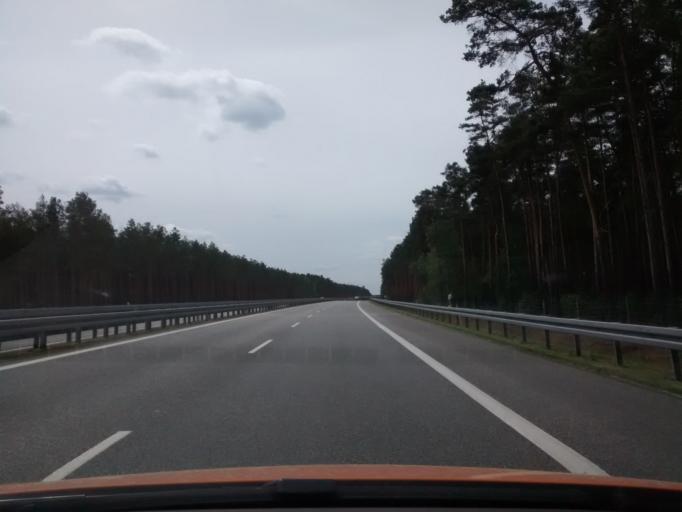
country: DE
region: Brandenburg
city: Trebbin
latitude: 52.1517
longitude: 13.2389
